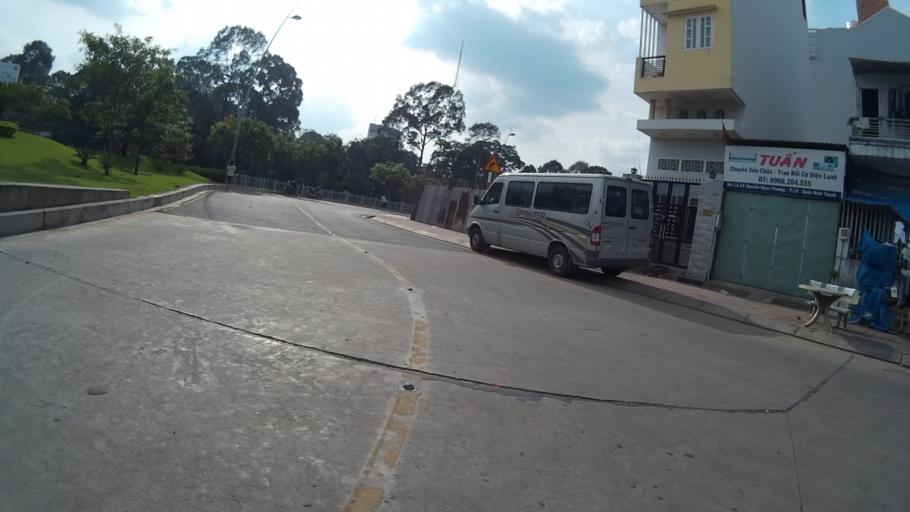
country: VN
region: Ho Chi Minh City
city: Quan Mot
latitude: 10.7879
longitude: 106.7095
